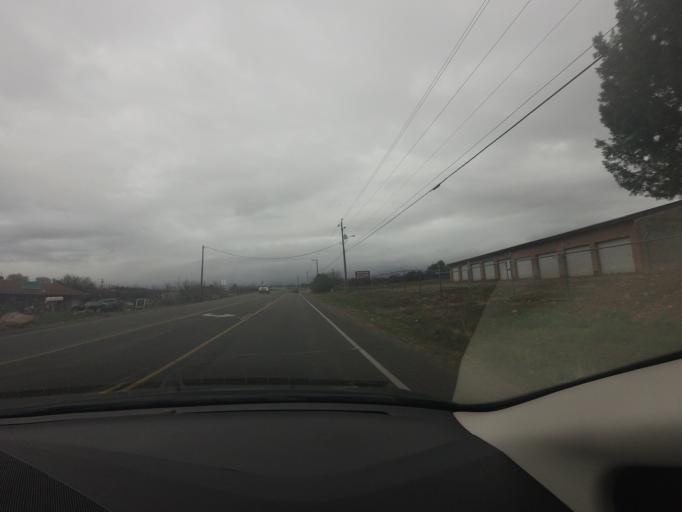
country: US
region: Arizona
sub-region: Yavapai County
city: Lake Montezuma
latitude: 34.6435
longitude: -111.7907
